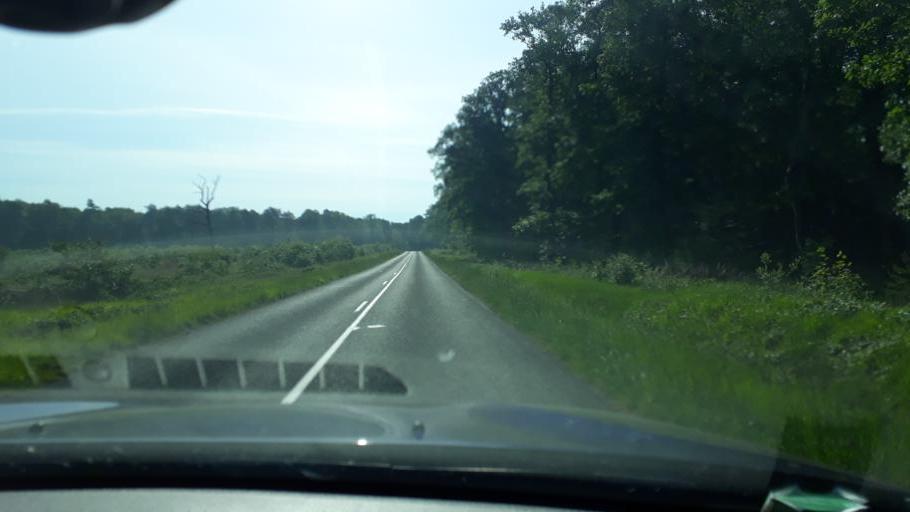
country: FR
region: Centre
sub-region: Departement du Loiret
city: Dadonville
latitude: 48.0599
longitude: 2.2470
